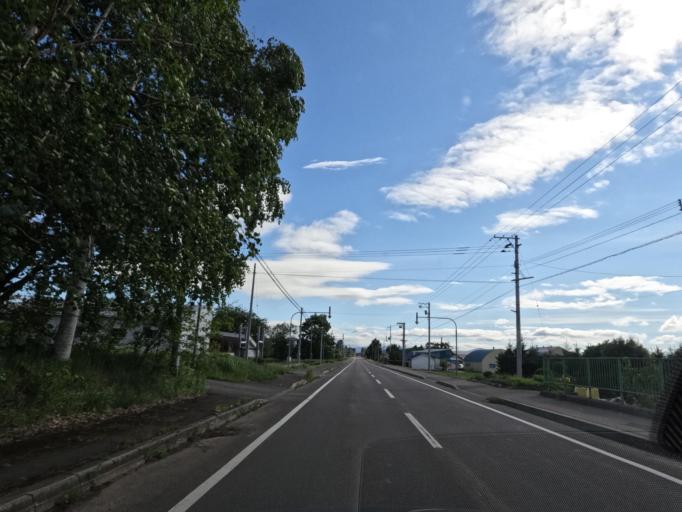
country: JP
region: Hokkaido
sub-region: Asahikawa-shi
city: Asahikawa
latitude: 43.7052
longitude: 142.5157
